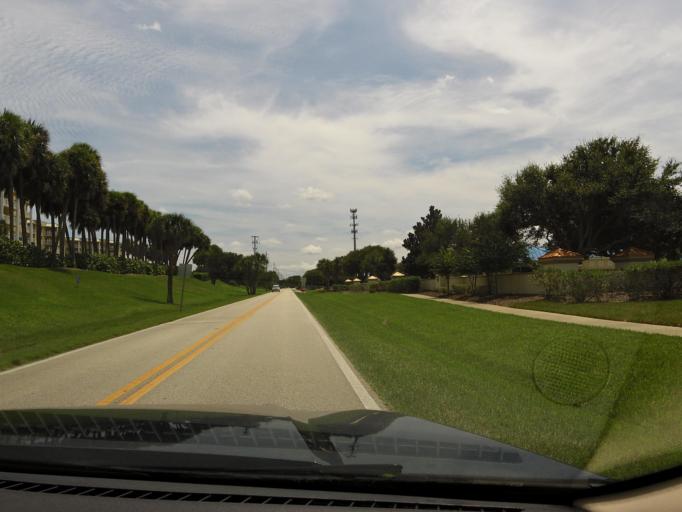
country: US
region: Florida
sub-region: Volusia County
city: Ponce Inlet
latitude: 29.1010
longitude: -80.9419
